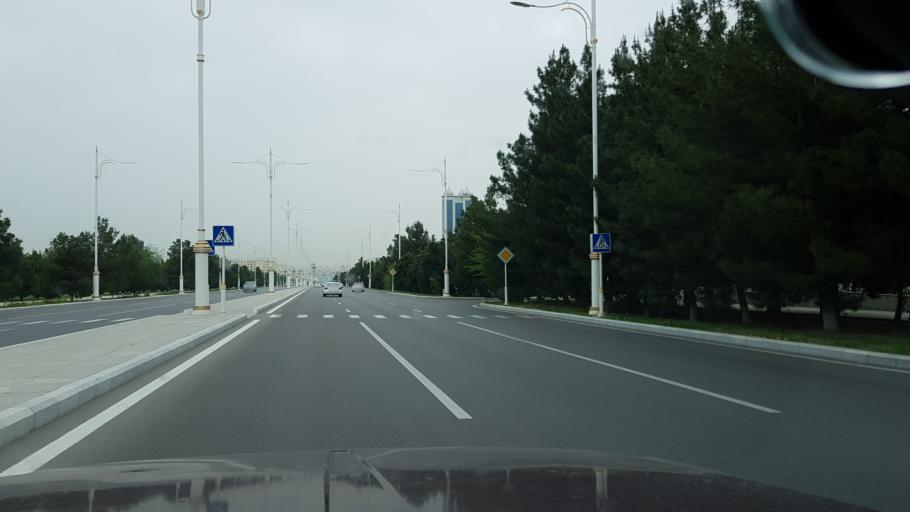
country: TM
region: Ahal
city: Ashgabat
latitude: 37.8881
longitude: 58.3878
